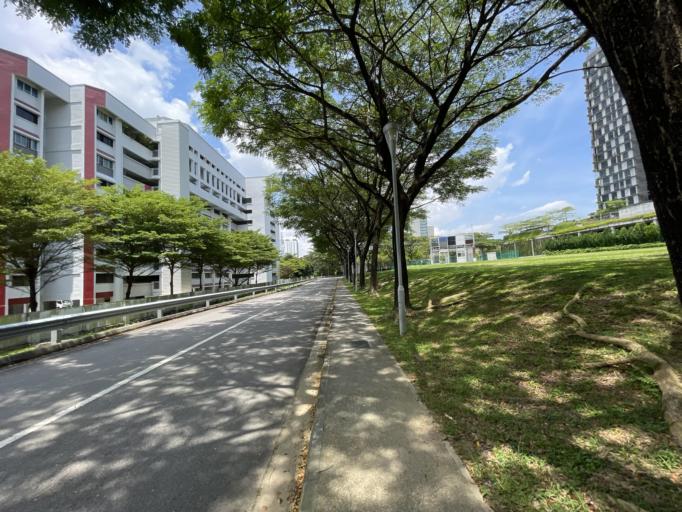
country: SG
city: Singapore
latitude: 1.3033
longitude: 103.7691
